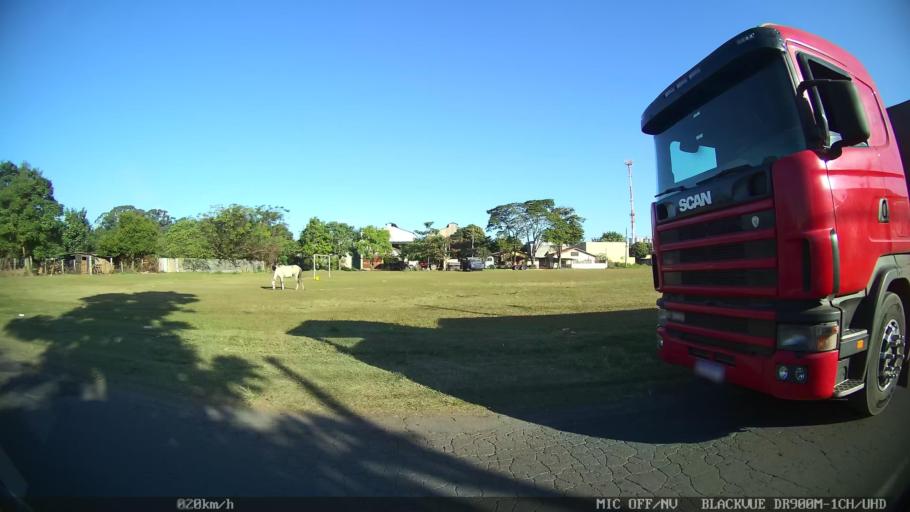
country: BR
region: Sao Paulo
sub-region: Nova Odessa
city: Nova Odessa
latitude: -22.7755
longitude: -47.2889
